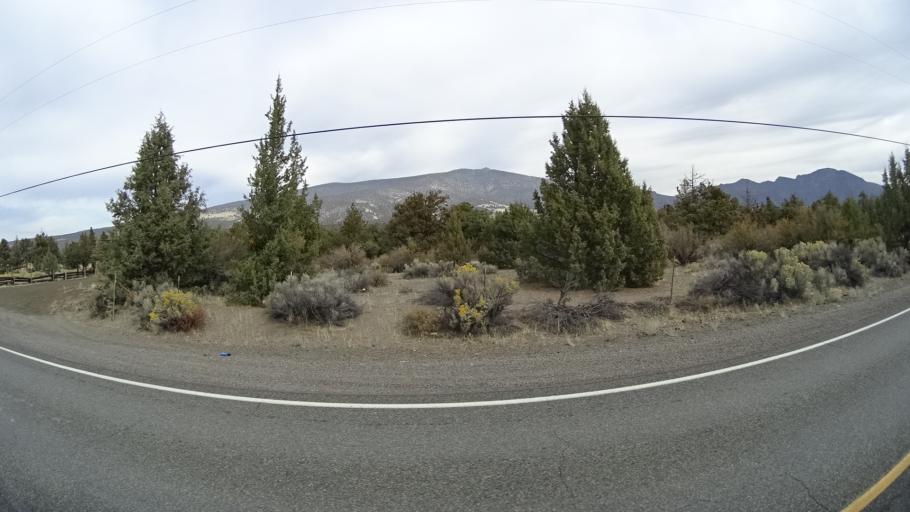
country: US
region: California
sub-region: Siskiyou County
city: Weed
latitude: 41.5825
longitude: -122.2923
